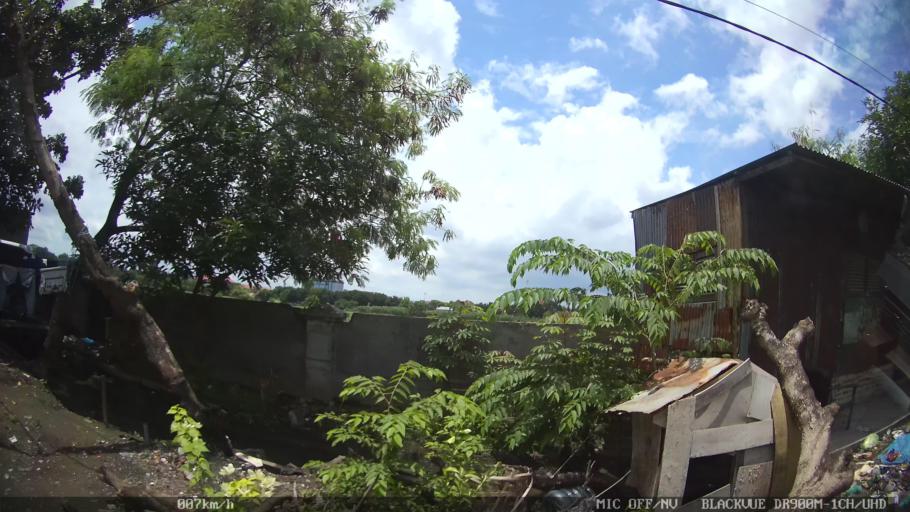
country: ID
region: North Sumatra
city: Medan
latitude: 3.6133
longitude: 98.7211
